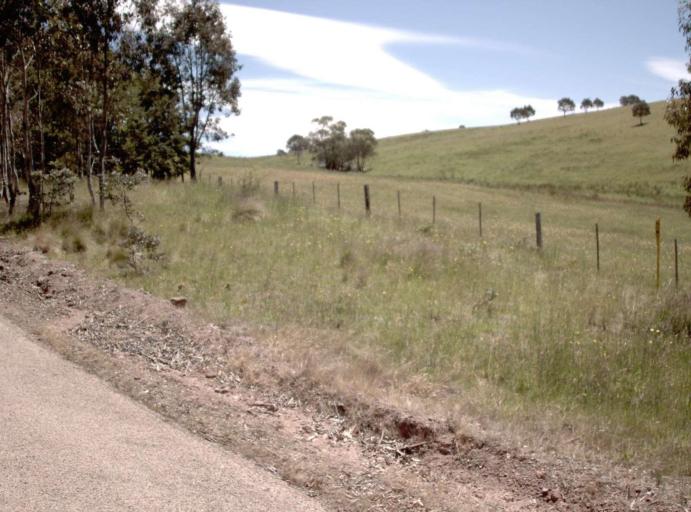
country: AU
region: New South Wales
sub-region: Snowy River
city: Jindabyne
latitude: -37.0588
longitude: 148.2600
